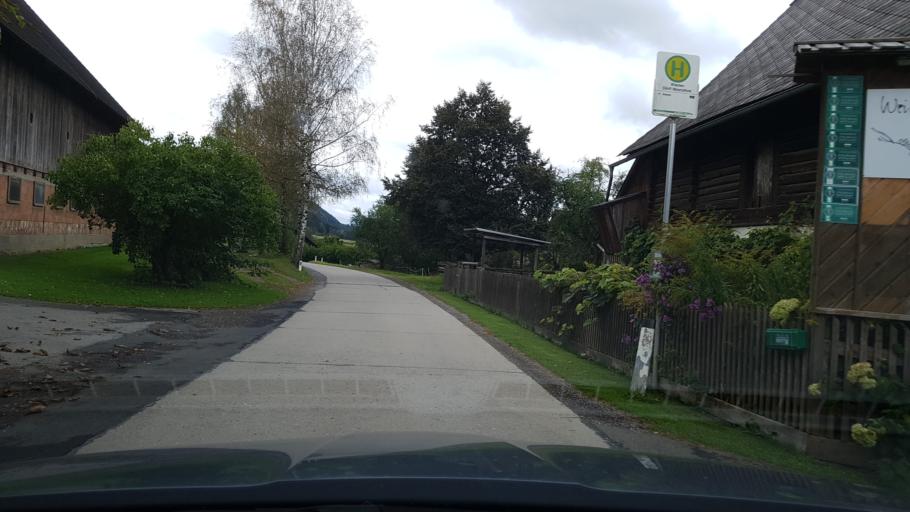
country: AT
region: Styria
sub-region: Politischer Bezirk Bruck-Muerzzuschlag
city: Allerheiligen im Muerztal
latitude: 47.4754
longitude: 15.4013
